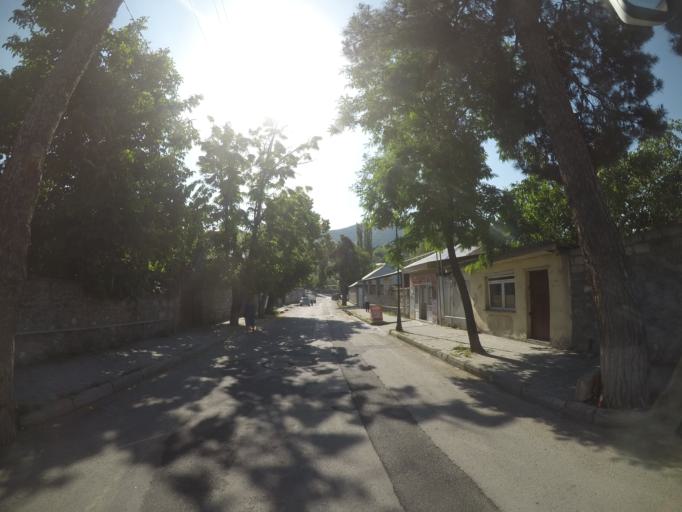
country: AZ
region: Shaki City
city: Sheki
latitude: 41.2009
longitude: 47.1780
